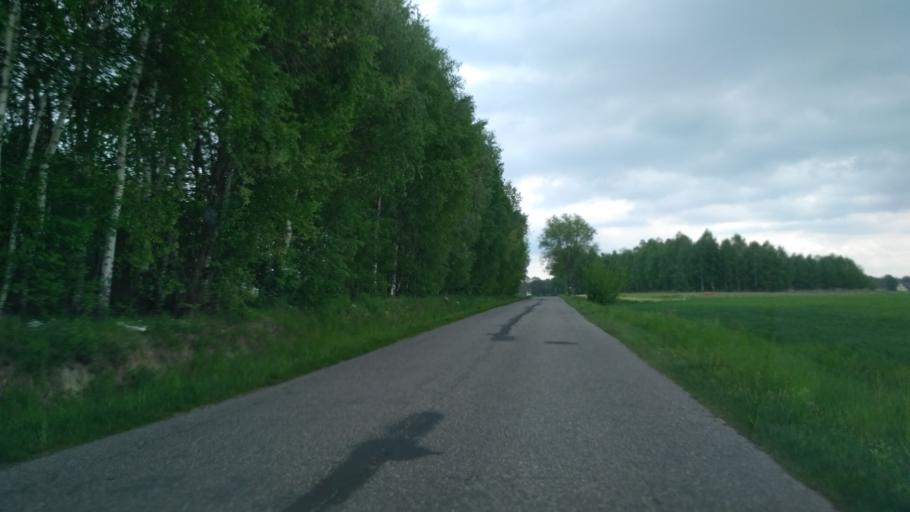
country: PL
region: Lesser Poland Voivodeship
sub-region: Powiat tarnowski
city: Szynwald
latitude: 49.9835
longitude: 21.1350
